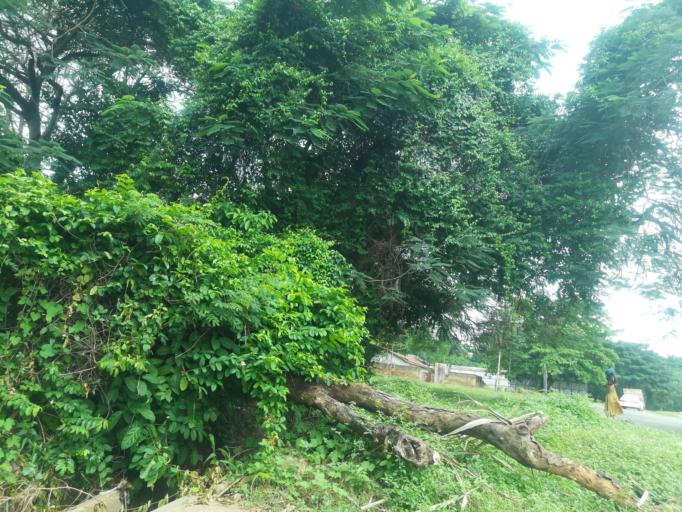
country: NG
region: Oyo
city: Ibadan
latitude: 7.4416
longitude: 3.9024
